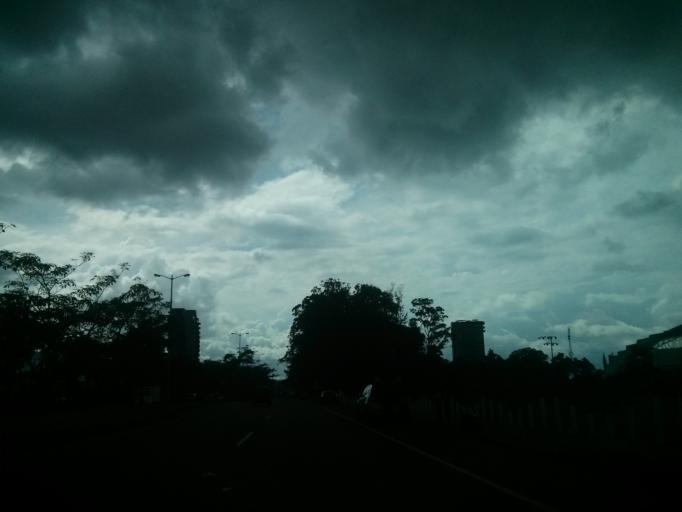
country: CR
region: San Jose
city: San Jose
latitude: 9.9333
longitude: -84.1047
